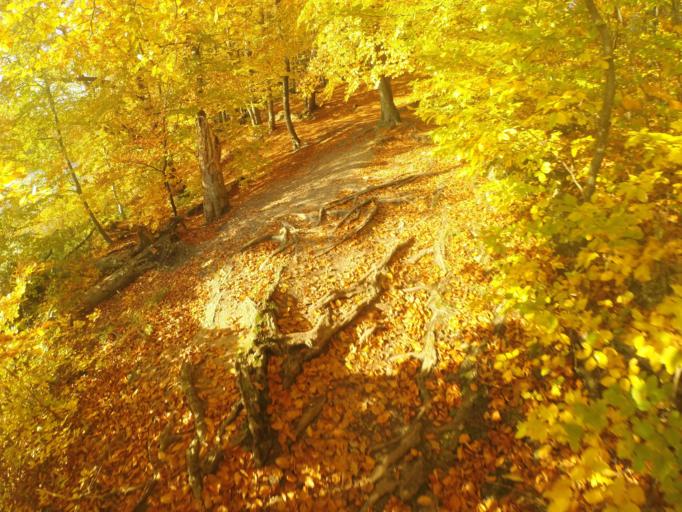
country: DK
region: Capital Region
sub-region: Rudersdal Kommune
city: Holte
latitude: 55.7774
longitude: 12.4410
